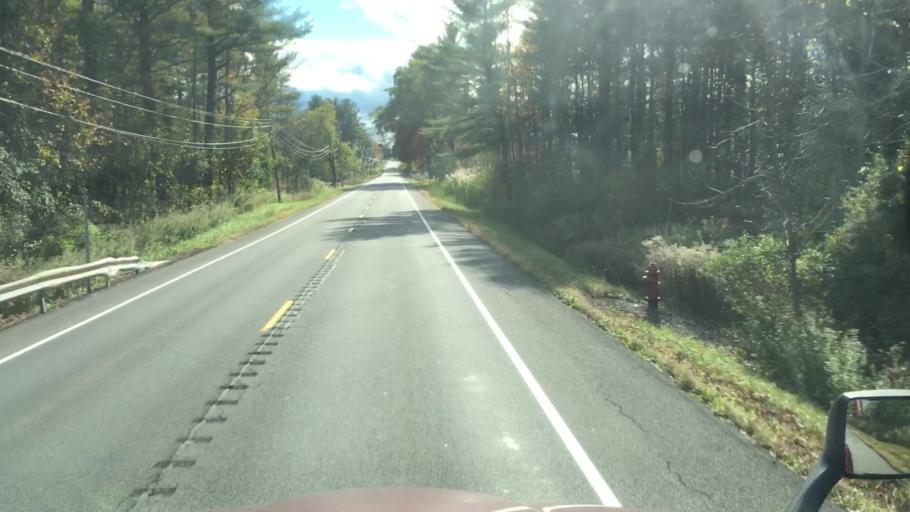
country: US
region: New York
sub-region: Saratoga County
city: Ballston Spa
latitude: 42.9453
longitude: -73.8700
